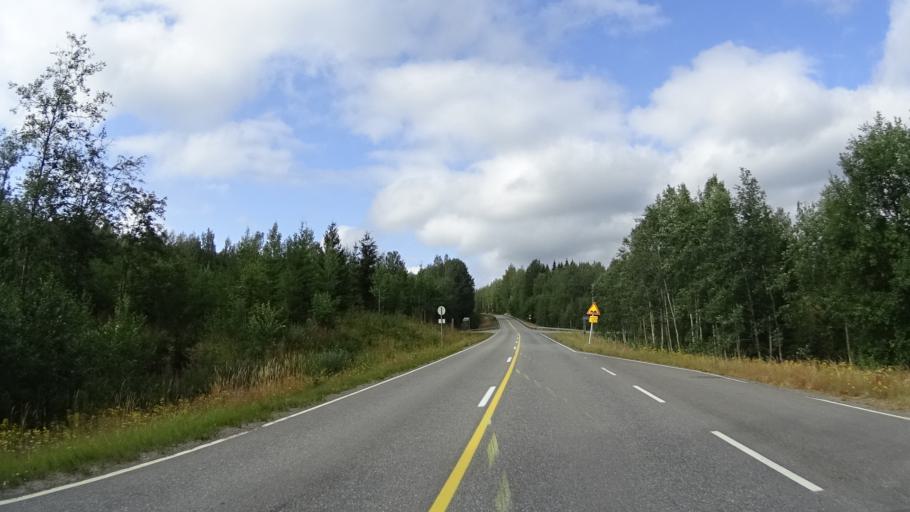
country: FI
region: Pirkanmaa
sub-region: Tampere
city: Luopioinen
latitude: 61.4954
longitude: 24.7877
